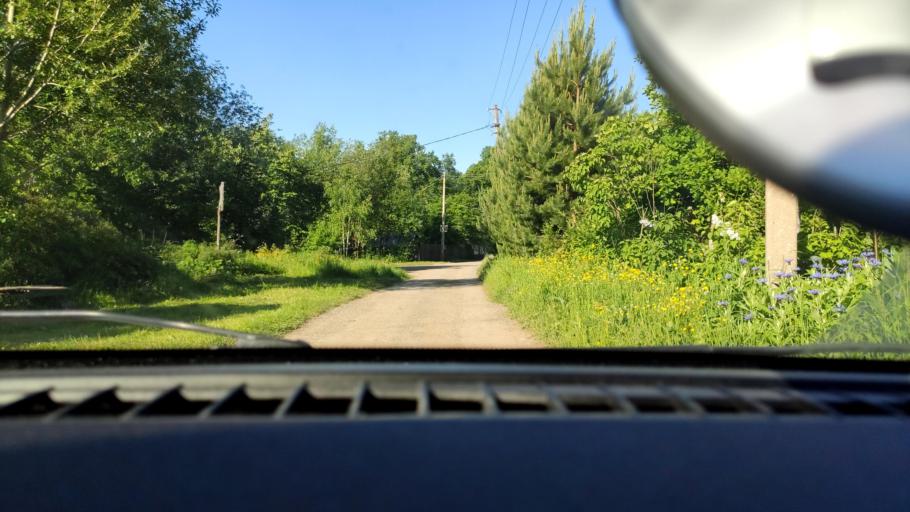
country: RU
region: Perm
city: Novyye Lyady
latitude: 58.1746
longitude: 56.5961
